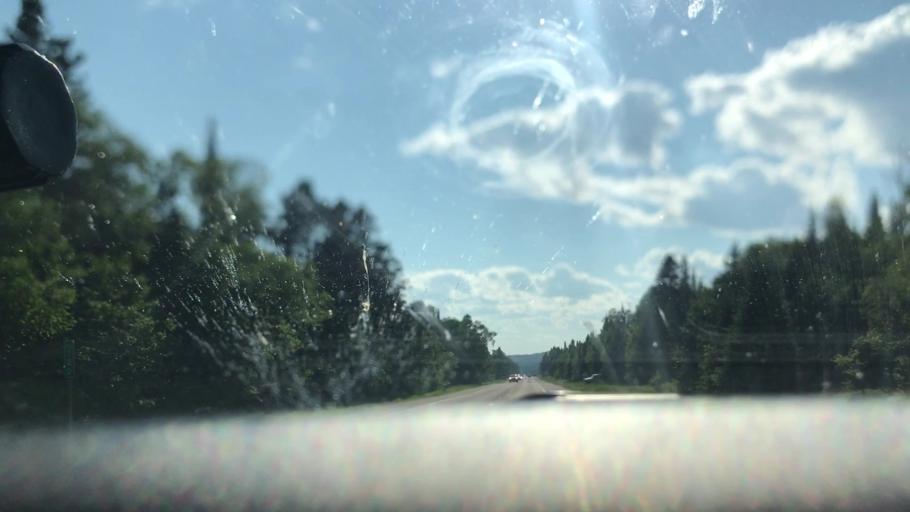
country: US
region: Minnesota
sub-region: Cook County
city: Grand Marais
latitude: 47.7961
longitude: -90.1306
